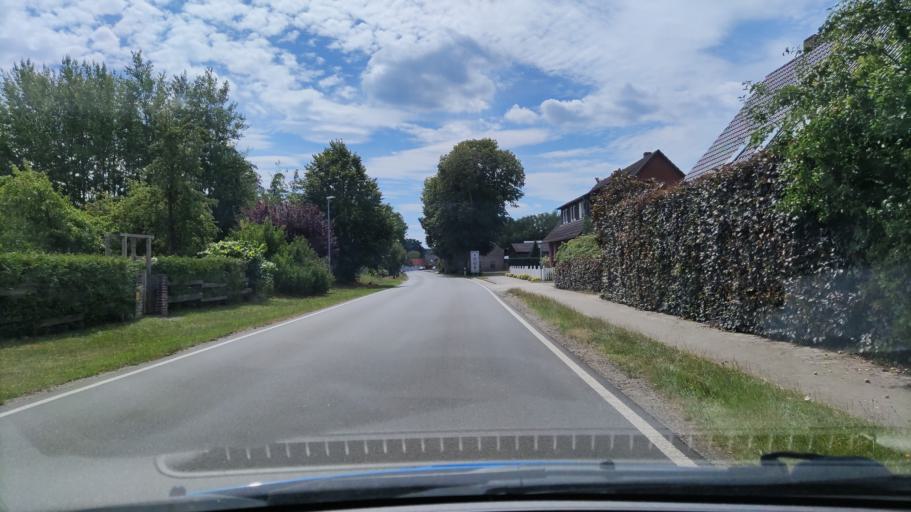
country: DE
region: Lower Saxony
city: Clenze
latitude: 52.9160
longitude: 10.9470
